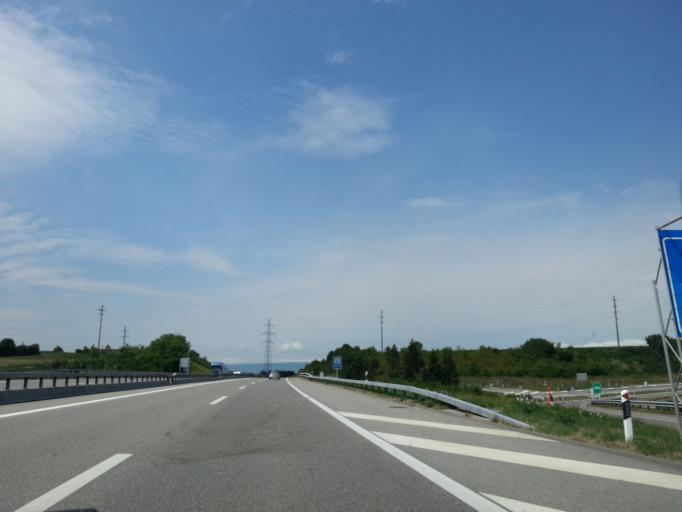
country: CH
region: Fribourg
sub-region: See District
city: Kerzers
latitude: 46.9609
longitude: 7.1938
